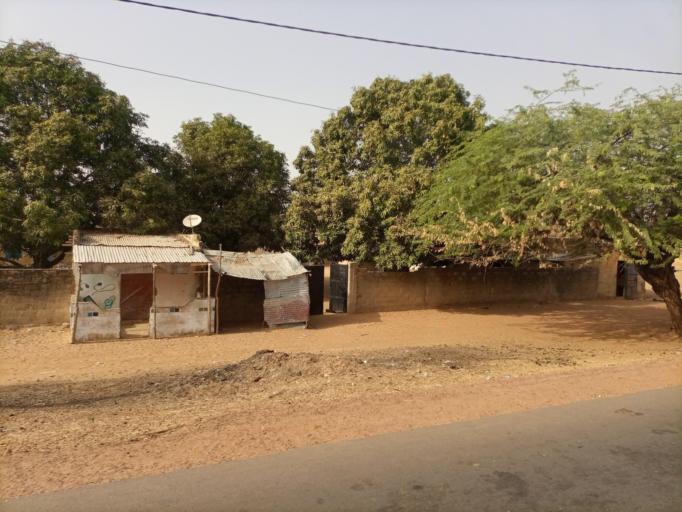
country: SN
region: Fatick
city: Foundiougne
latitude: 14.1210
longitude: -16.4382
